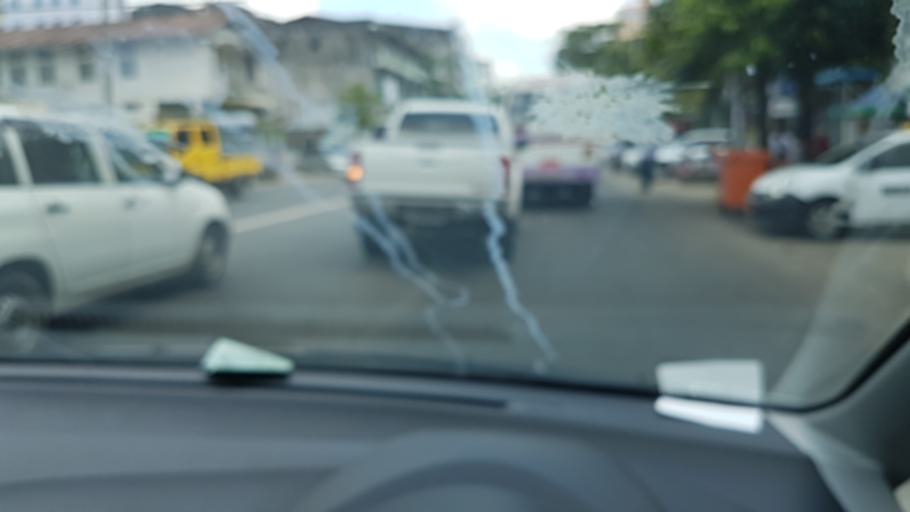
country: MM
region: Yangon
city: Yangon
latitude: 16.7868
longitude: 96.1677
